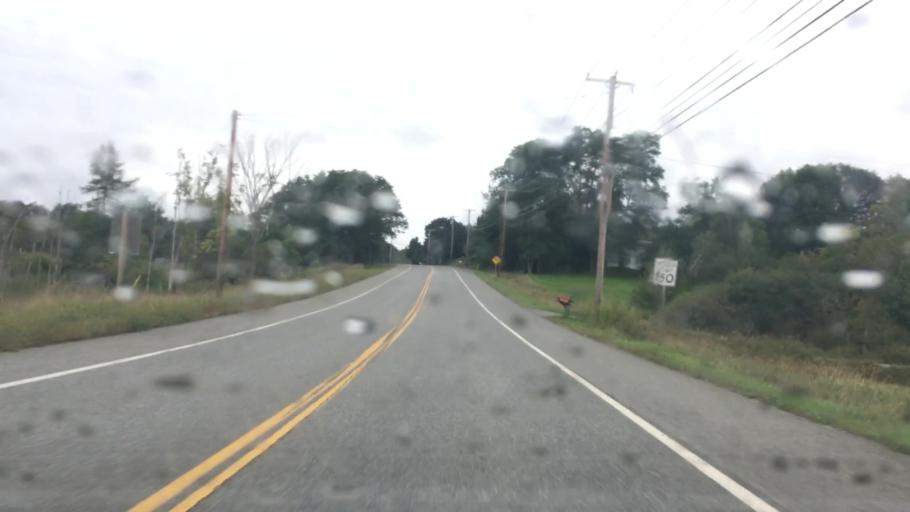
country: US
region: Maine
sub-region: Penobscot County
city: Orrington
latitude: 44.7174
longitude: -68.8270
